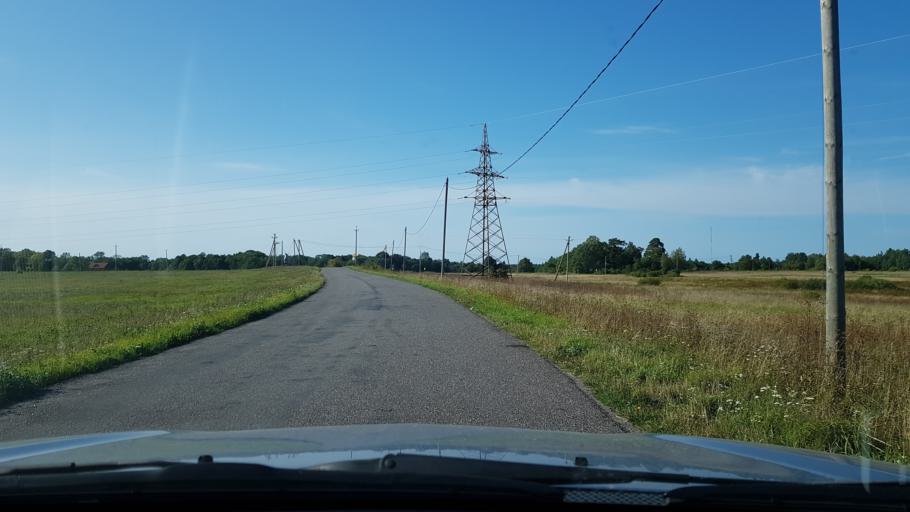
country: EE
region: Ida-Virumaa
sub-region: Narva-Joesuu linn
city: Narva-Joesuu
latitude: 59.4078
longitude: 28.0294
